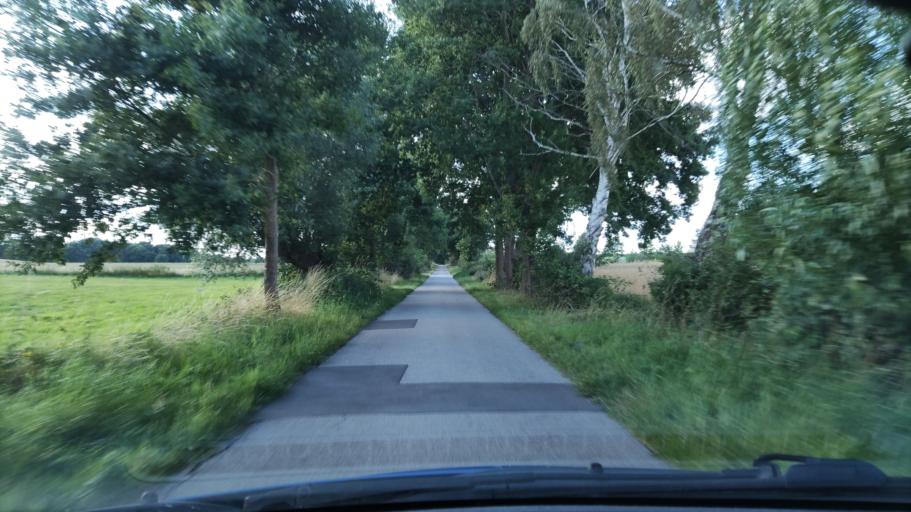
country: DE
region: Lower Saxony
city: Dahlenburg
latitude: 53.1809
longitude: 10.6895
